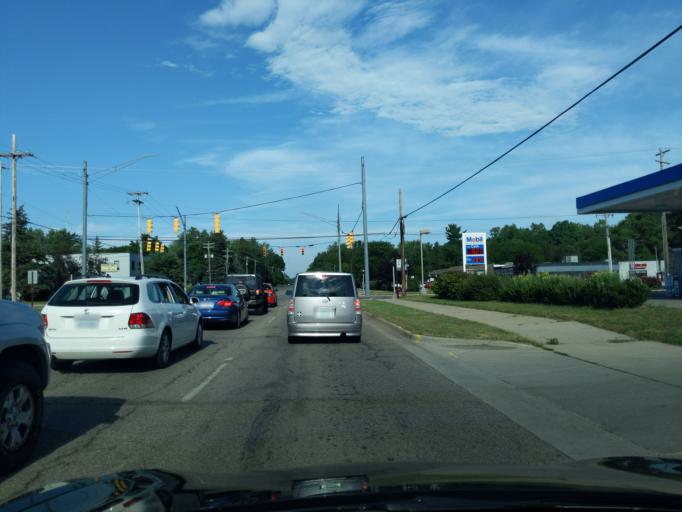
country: US
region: Michigan
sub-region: Ingham County
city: Okemos
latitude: 42.7470
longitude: -84.4284
